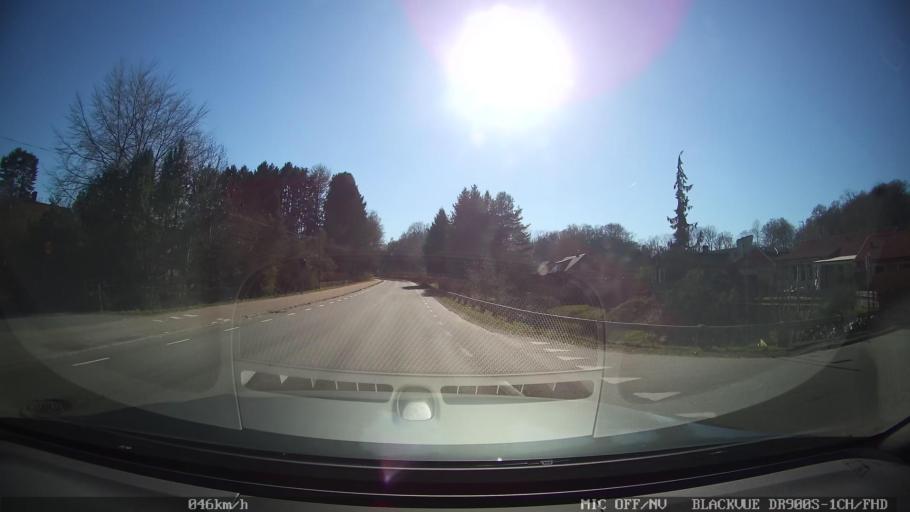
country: SE
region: Skane
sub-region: Klippans Kommun
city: Ljungbyhed
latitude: 55.9982
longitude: 13.2861
